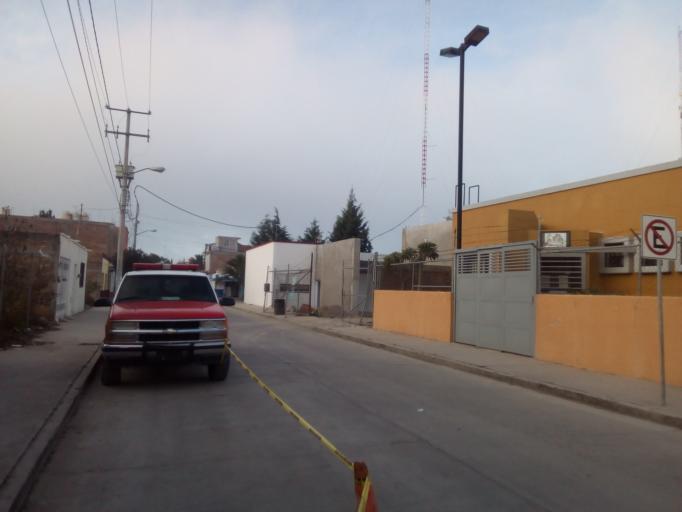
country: MX
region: Guanajuato
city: San Jose Iturbide
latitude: 21.0067
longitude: -100.3889
